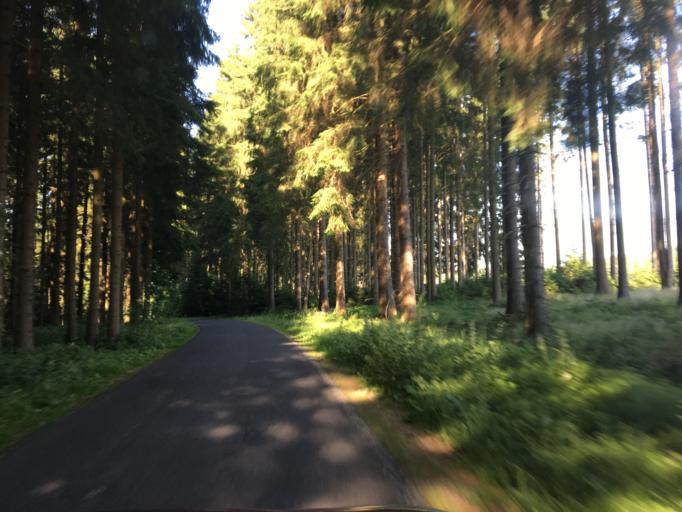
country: AT
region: Upper Austria
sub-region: Politischer Bezirk Urfahr-Umgebung
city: Oberneukirchen
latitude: 48.5031
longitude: 14.2286
